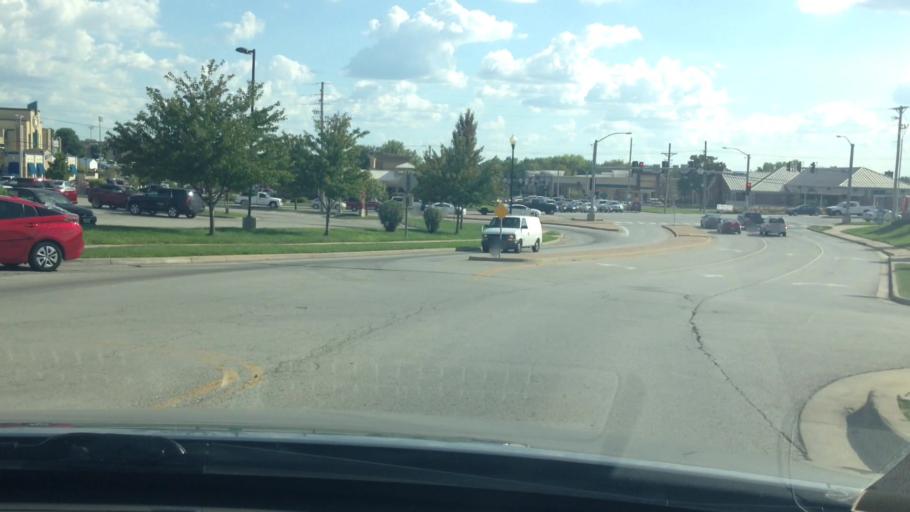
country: US
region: Missouri
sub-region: Clay County
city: Liberty
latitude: 39.2457
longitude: -94.4510
